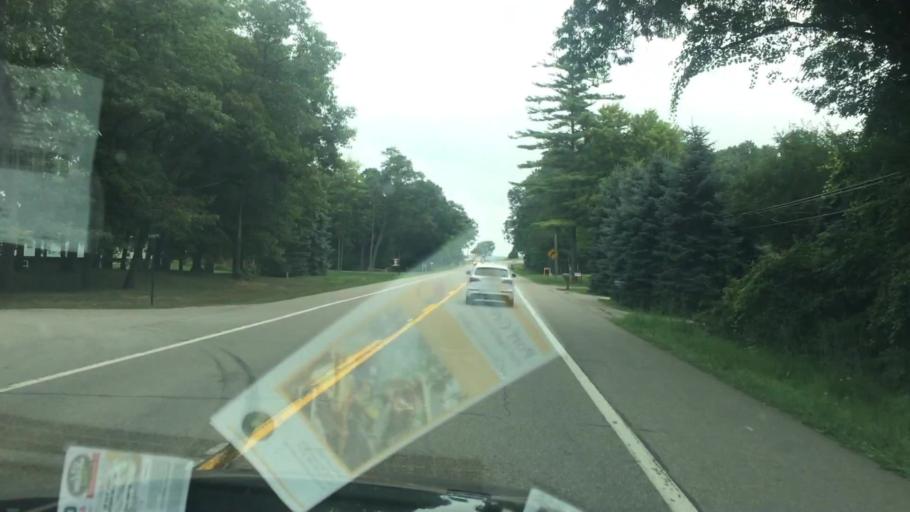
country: US
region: Michigan
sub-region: Huron County
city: Pigeon
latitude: 43.9846
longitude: -83.1691
